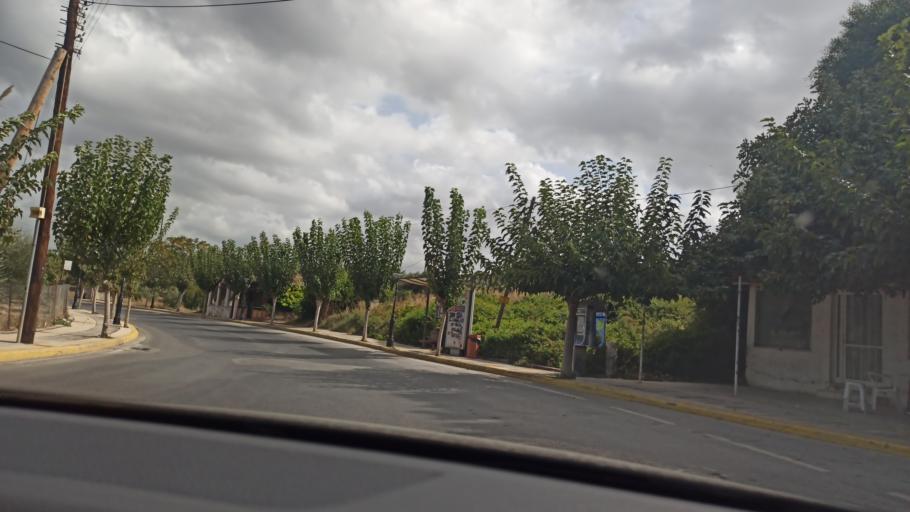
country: GR
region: Crete
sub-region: Nomos Irakleiou
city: Gazi
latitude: 35.3348
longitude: 25.0574
